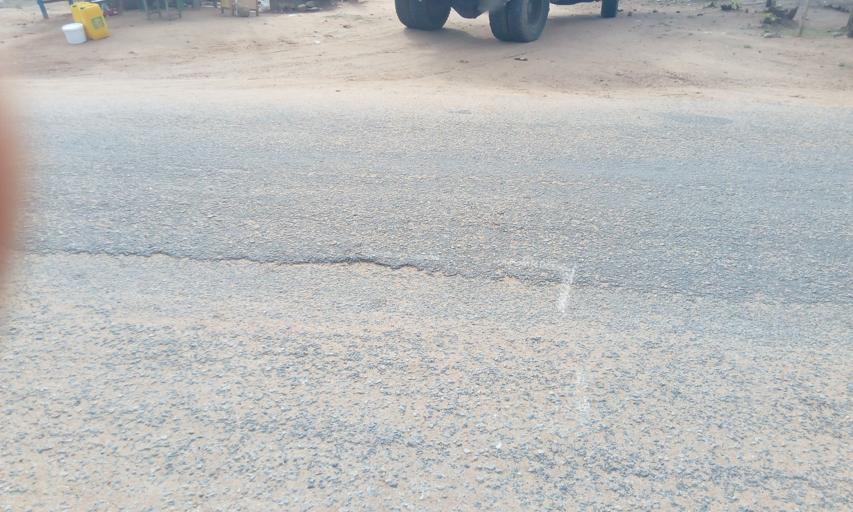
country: GH
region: Central
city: Winneba
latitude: 5.3592
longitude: -0.6232
